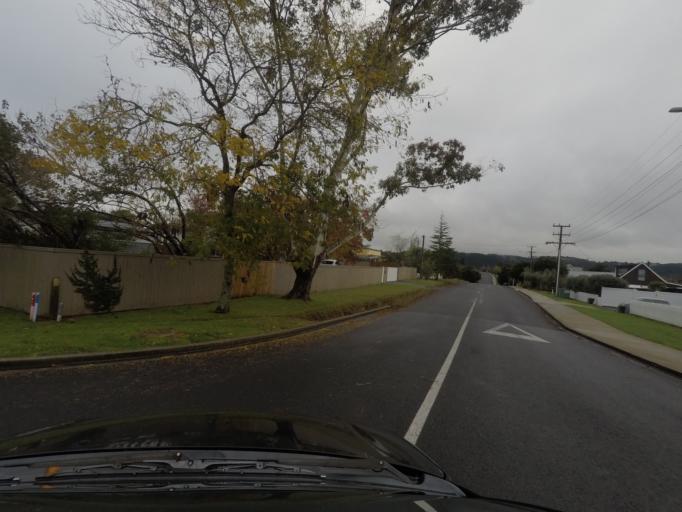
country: NZ
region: Auckland
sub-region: Auckland
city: Rosebank
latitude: -36.7632
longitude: 174.5933
